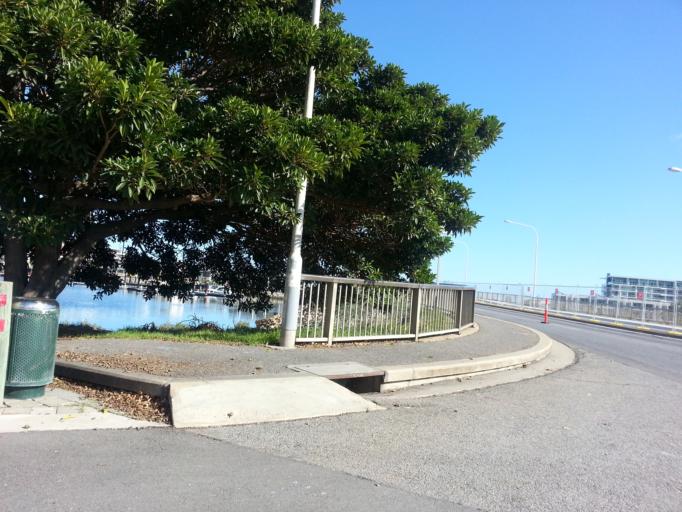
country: AU
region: South Australia
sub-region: Port Adelaide Enfield
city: Birkenhead
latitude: -34.8459
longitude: 138.4984
